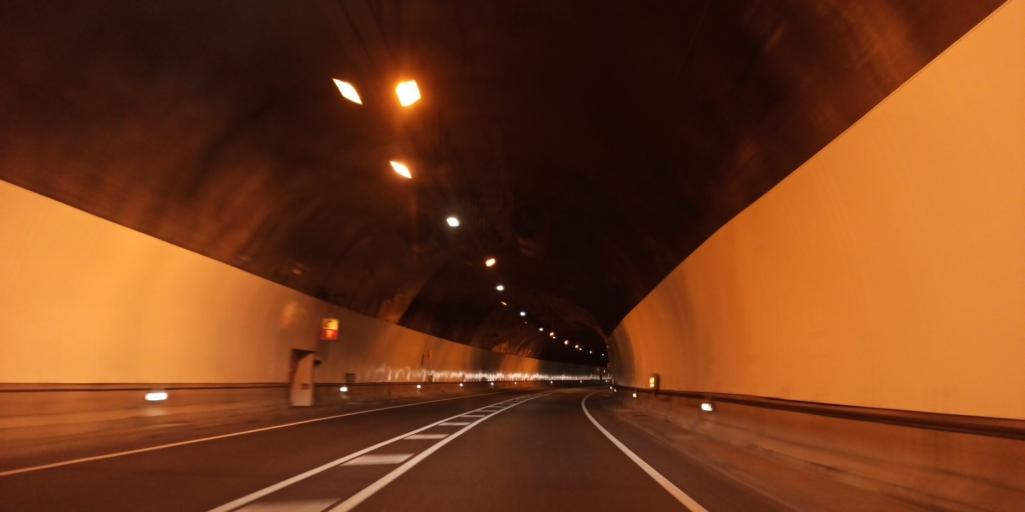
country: ES
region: Catalonia
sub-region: Provincia de Girona
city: Bas
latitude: 42.1245
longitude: 2.4580
